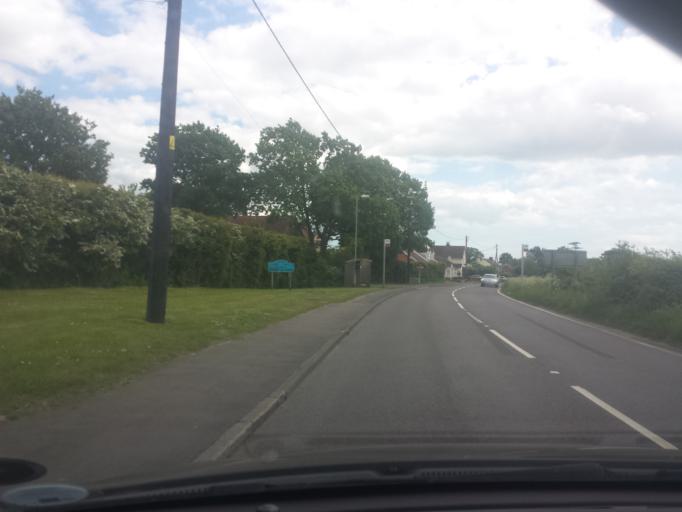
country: GB
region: England
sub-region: Essex
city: Little Clacton
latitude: 51.8635
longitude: 1.1528
